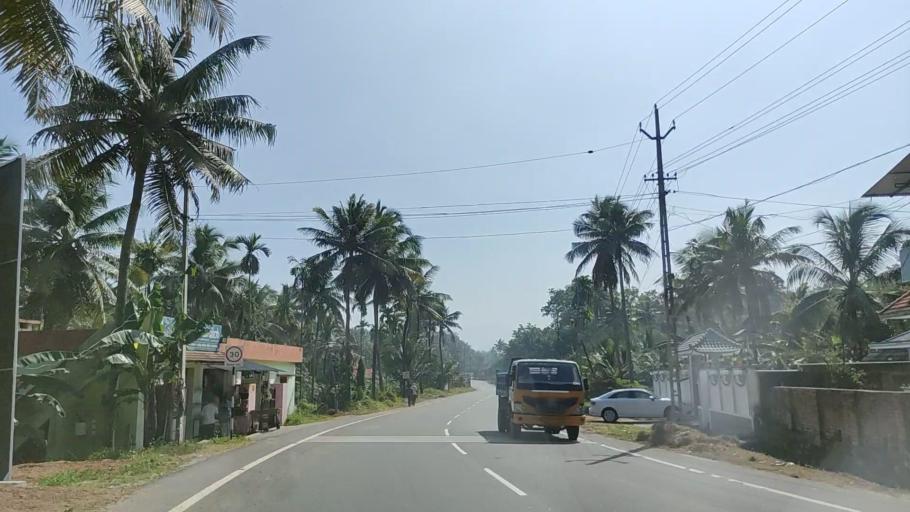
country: IN
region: Kerala
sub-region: Kollam
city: Punalur
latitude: 8.9186
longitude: 77.0391
